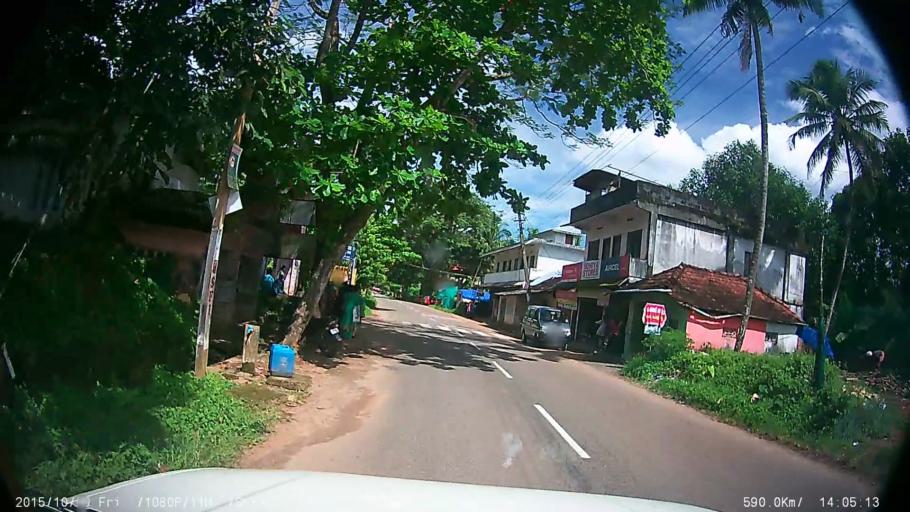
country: IN
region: Kerala
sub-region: Ernakulam
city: Piravam
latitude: 9.8866
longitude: 76.5654
